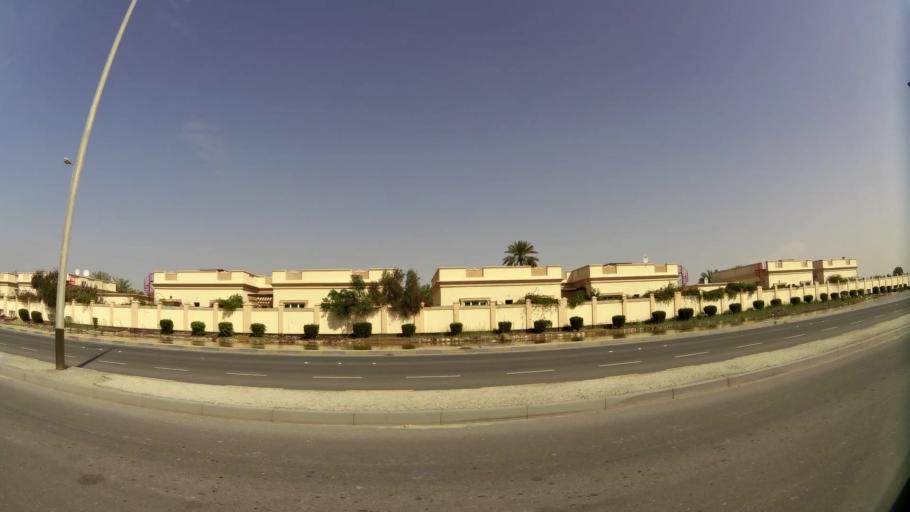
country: BH
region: Central Governorate
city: Madinat Hamad
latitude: 26.1852
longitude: 50.4658
